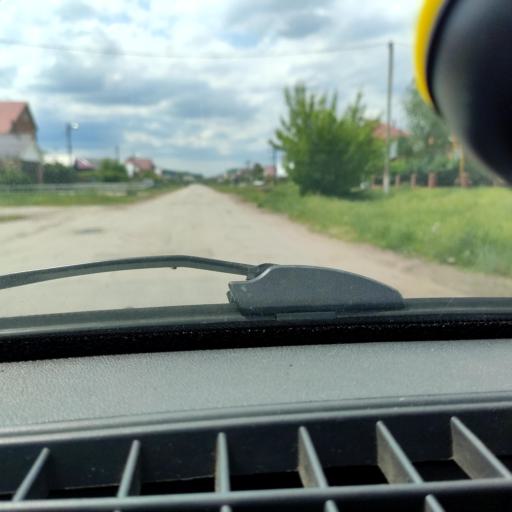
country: RU
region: Samara
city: Povolzhskiy
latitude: 53.6396
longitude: 49.6823
